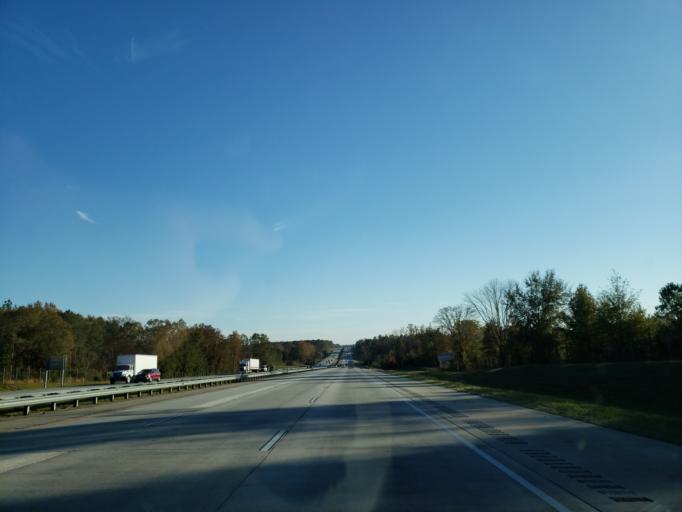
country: US
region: Georgia
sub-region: Dooly County
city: Unadilla
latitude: 32.3262
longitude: -83.7660
